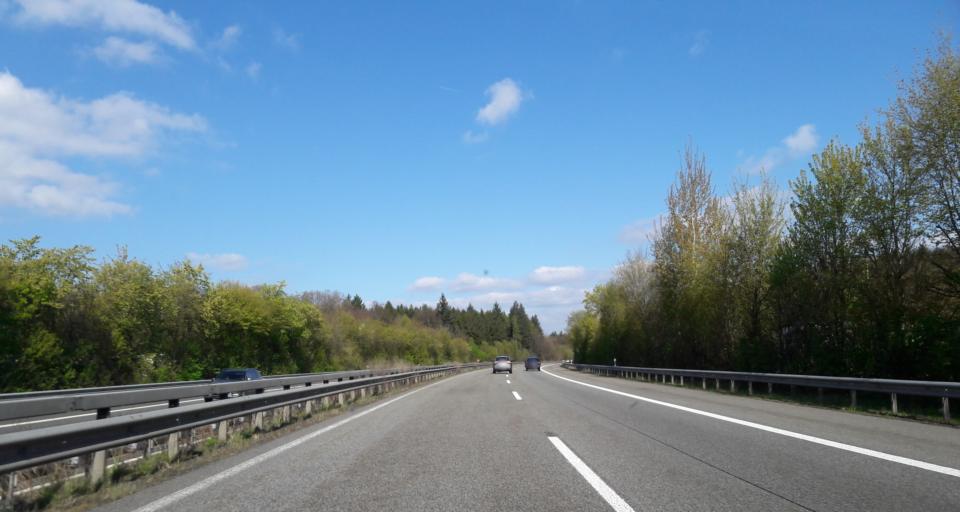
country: DE
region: Rheinland-Pfalz
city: Niederofflingen
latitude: 50.0688
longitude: 6.8817
